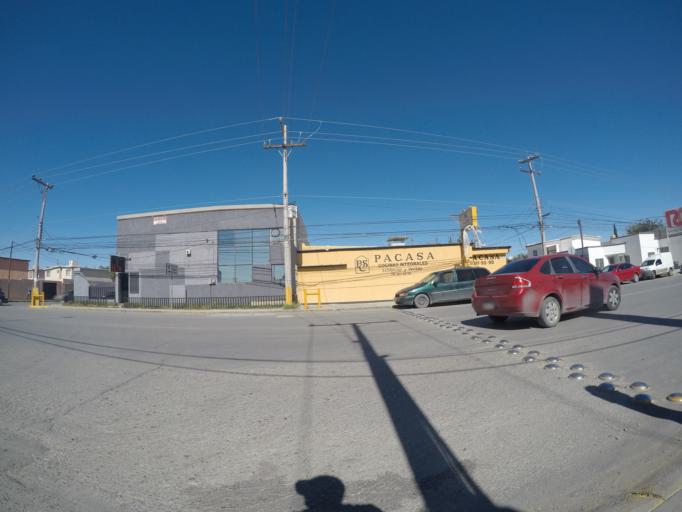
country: MX
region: Chihuahua
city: Ciudad Juarez
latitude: 31.7144
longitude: -106.4200
